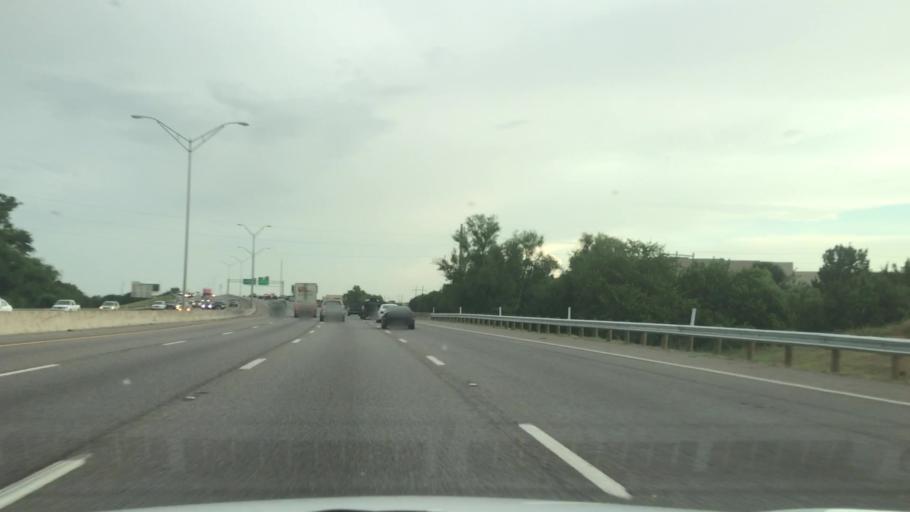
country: US
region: Texas
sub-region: Dallas County
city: Mesquite
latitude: 32.7764
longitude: -96.6244
